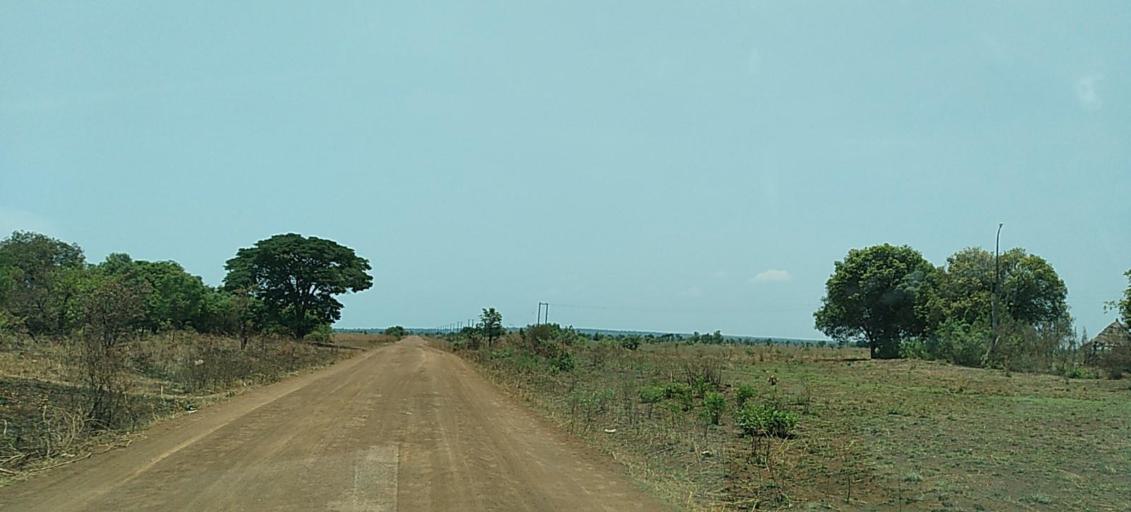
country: ZM
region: Copperbelt
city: Mpongwe
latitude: -13.6720
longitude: 27.8549
